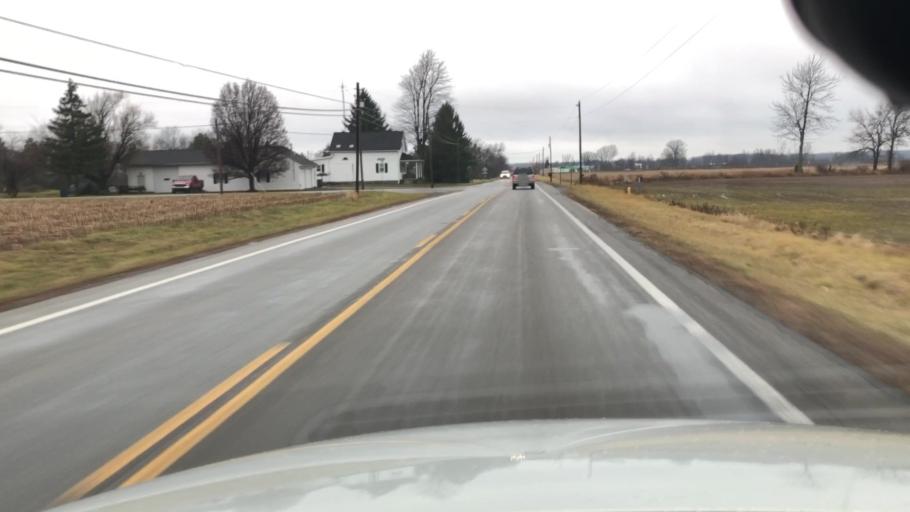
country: US
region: Ohio
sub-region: Allen County
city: Lima
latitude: 40.7035
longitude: -83.9979
